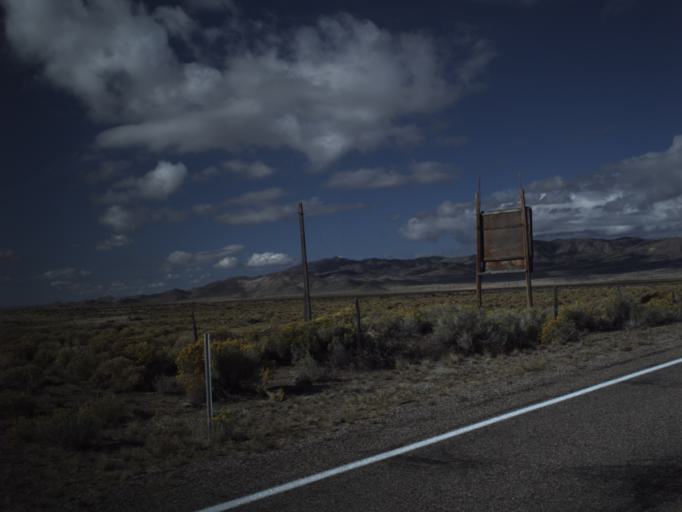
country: US
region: Utah
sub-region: Beaver County
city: Milford
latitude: 38.3971
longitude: -113.0224
